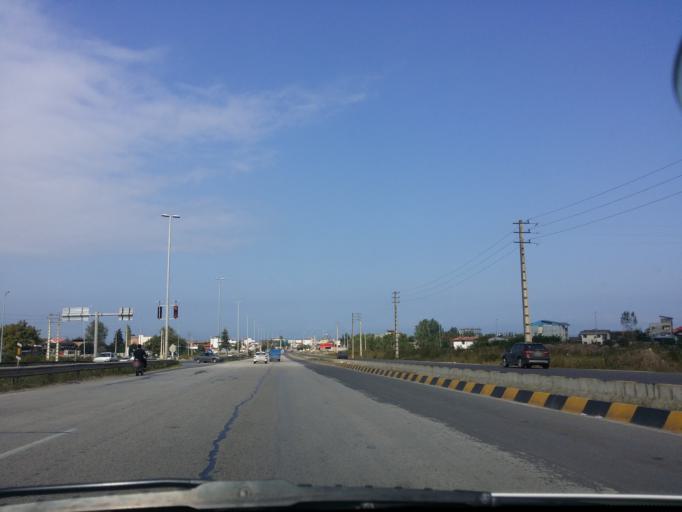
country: IR
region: Mazandaran
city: Chalus
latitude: 36.6544
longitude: 51.4038
